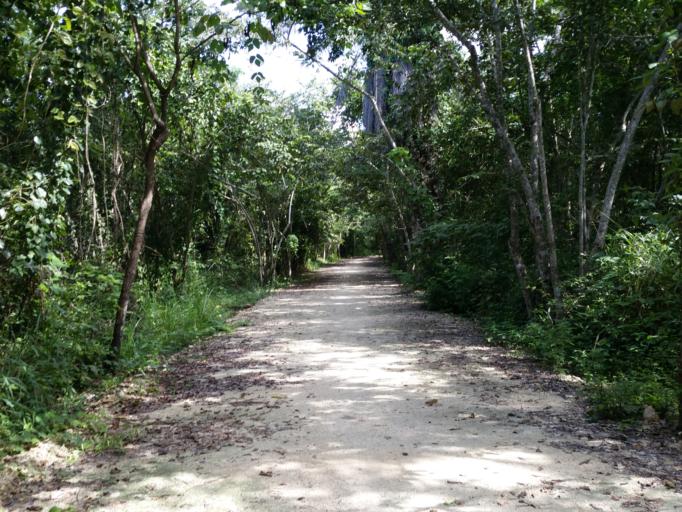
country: MX
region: Yucatan
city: Temozon
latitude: 20.8886
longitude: -88.1261
